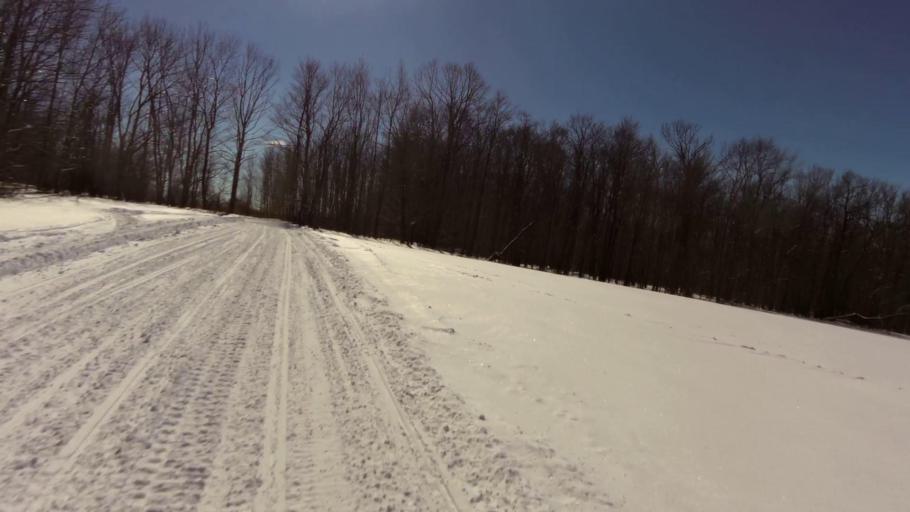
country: US
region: New York
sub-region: Chautauqua County
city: Mayville
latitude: 42.2339
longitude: -79.3940
